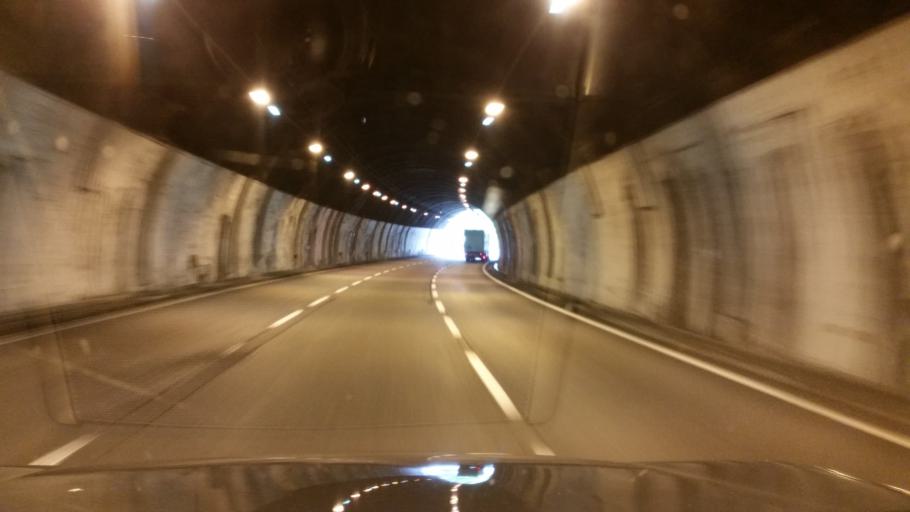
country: IT
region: Liguria
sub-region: Provincia di Genova
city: Masone
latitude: 44.4957
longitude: 8.7273
